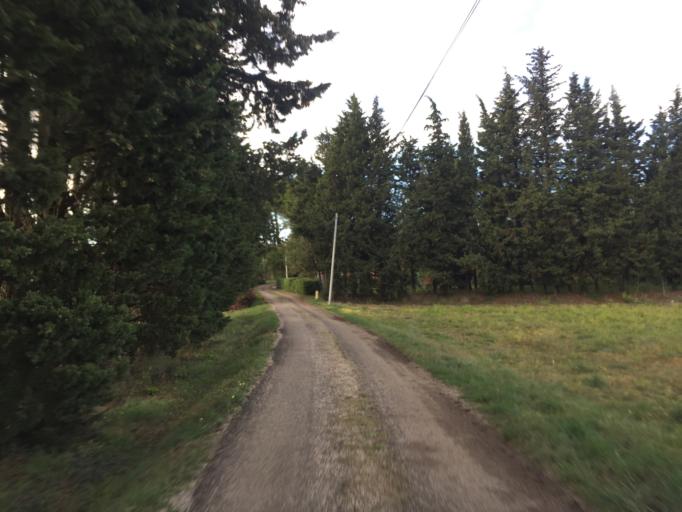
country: FR
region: Provence-Alpes-Cote d'Azur
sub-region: Departement du Vaucluse
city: Orange
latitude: 44.1110
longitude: 4.8116
